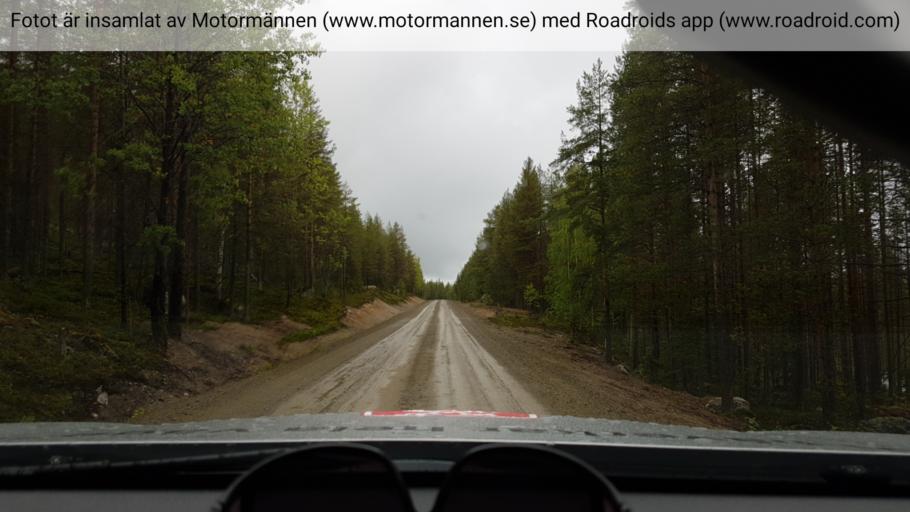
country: SE
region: Vaesterbotten
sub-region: Storumans Kommun
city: Storuman
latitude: 64.9558
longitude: 17.5590
